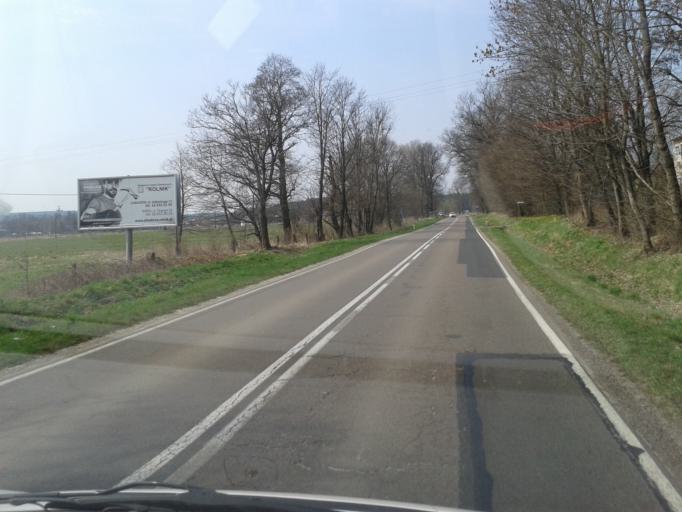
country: PL
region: Subcarpathian Voivodeship
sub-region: Powiat lubaczowski
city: Narol
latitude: 50.3594
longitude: 23.3367
